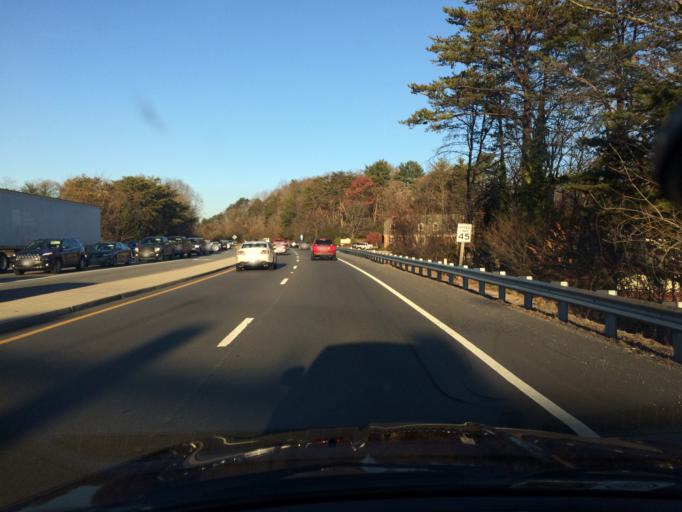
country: US
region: Virginia
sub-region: Roanoke County
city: Cave Spring
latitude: 37.2276
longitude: -80.0000
